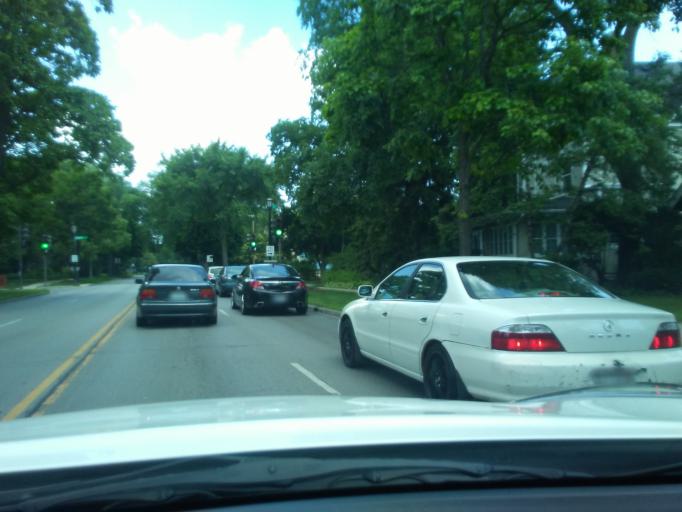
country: US
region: Illinois
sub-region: Cook County
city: Evanston
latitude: 42.0304
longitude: -87.6859
